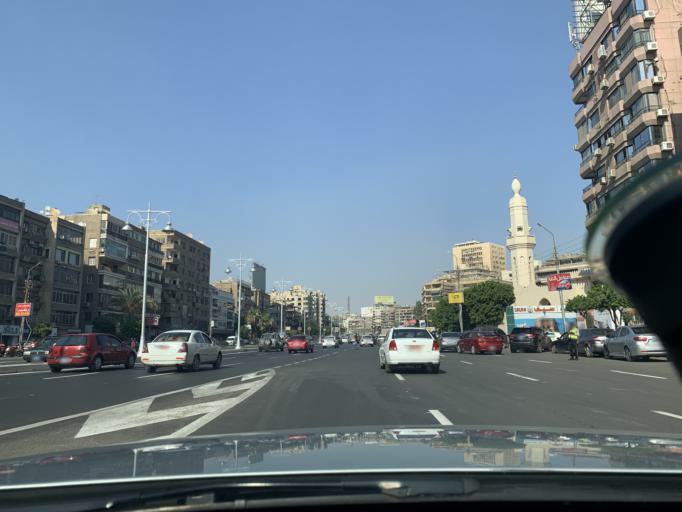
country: EG
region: Muhafazat al Qahirah
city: Cairo
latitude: 30.0842
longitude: 31.3273
